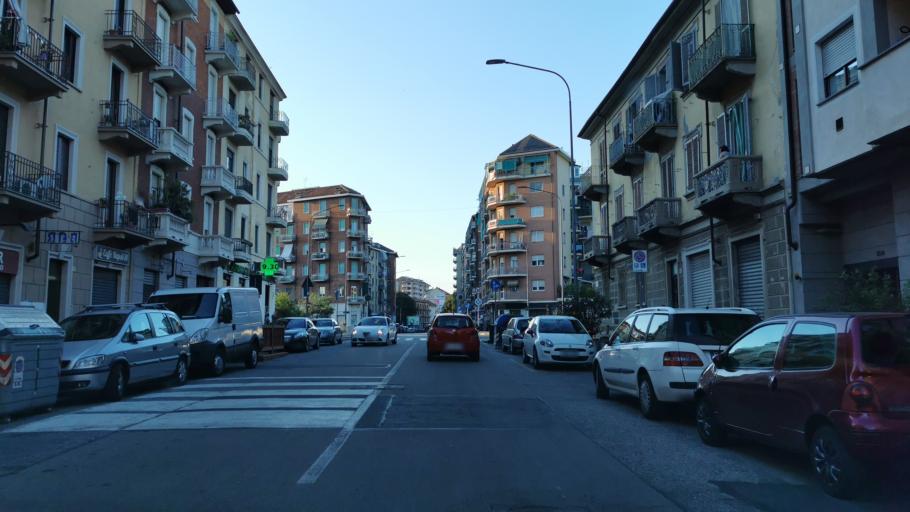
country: IT
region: Piedmont
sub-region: Provincia di Torino
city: Turin
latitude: 45.0980
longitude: 7.6940
